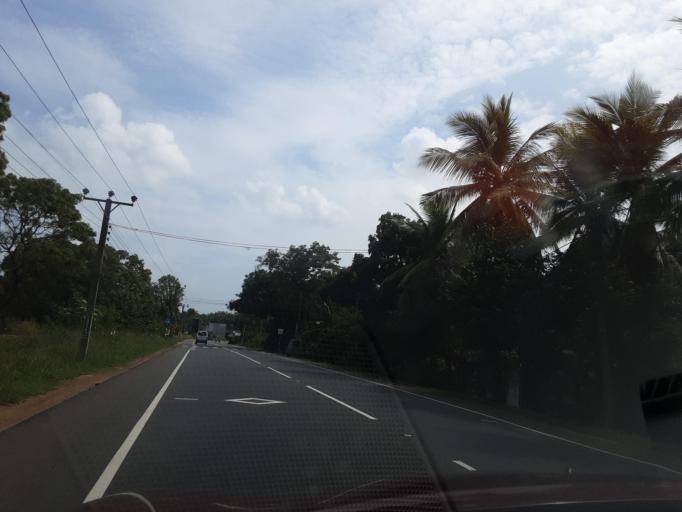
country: LK
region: North Central
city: Anuradhapura
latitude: 8.5034
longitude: 80.5103
